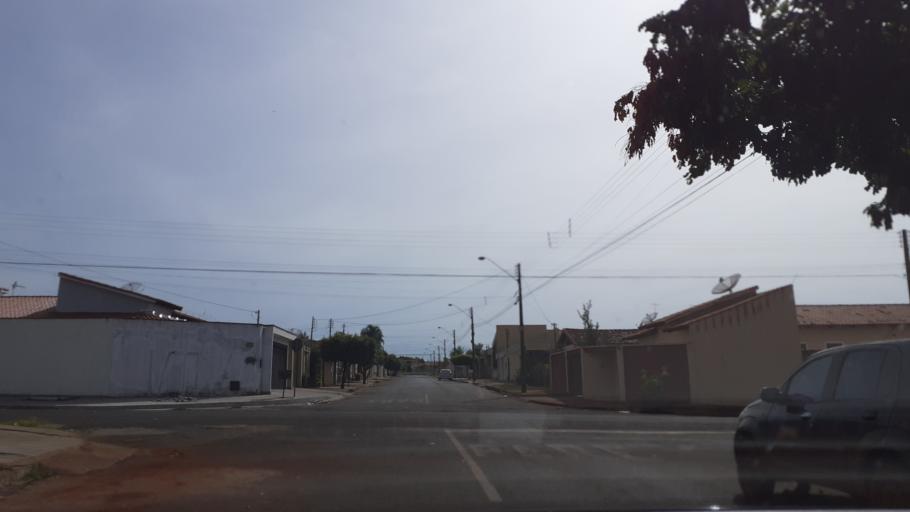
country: BR
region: Goias
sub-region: Itumbiara
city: Itumbiara
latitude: -18.4219
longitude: -49.2413
